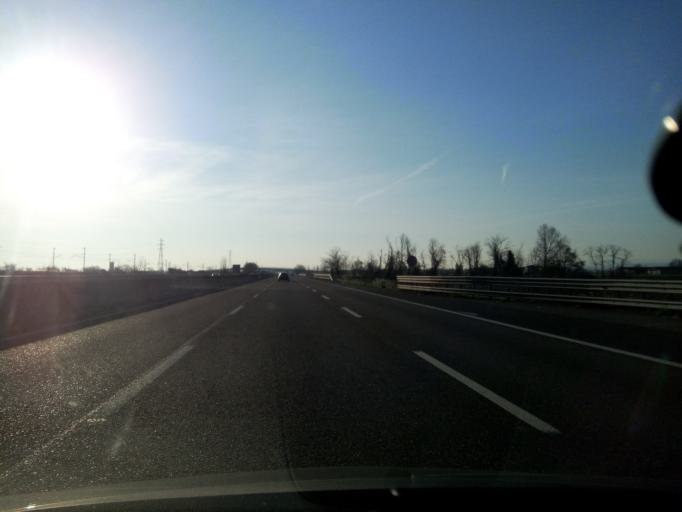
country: IT
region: Emilia-Romagna
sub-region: Provincia di Piacenza
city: Fiorenzuola d'Arda
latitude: 44.9535
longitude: 9.9267
